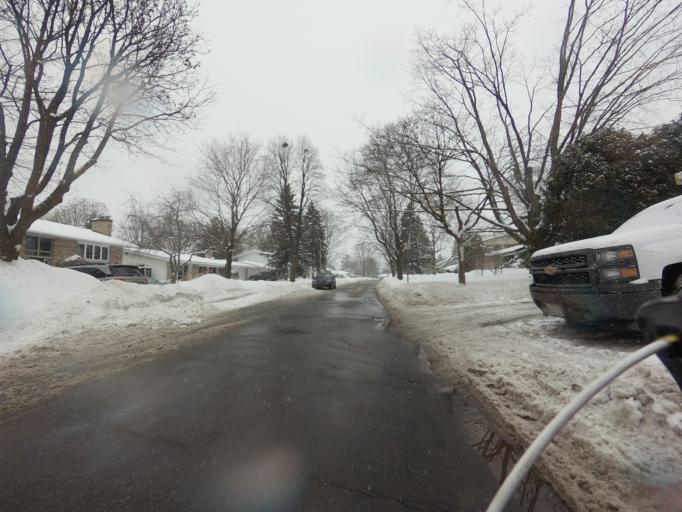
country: CA
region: Ontario
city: Ottawa
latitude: 45.3654
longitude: -75.7571
